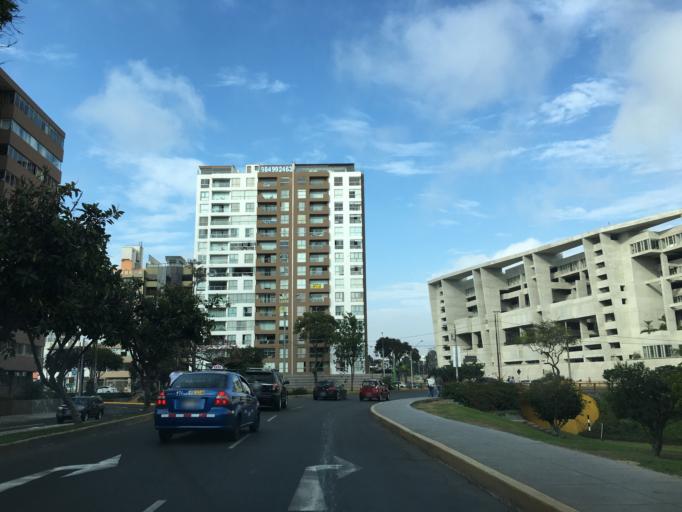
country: PE
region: Lima
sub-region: Lima
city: Surco
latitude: -12.1349
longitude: -77.0240
